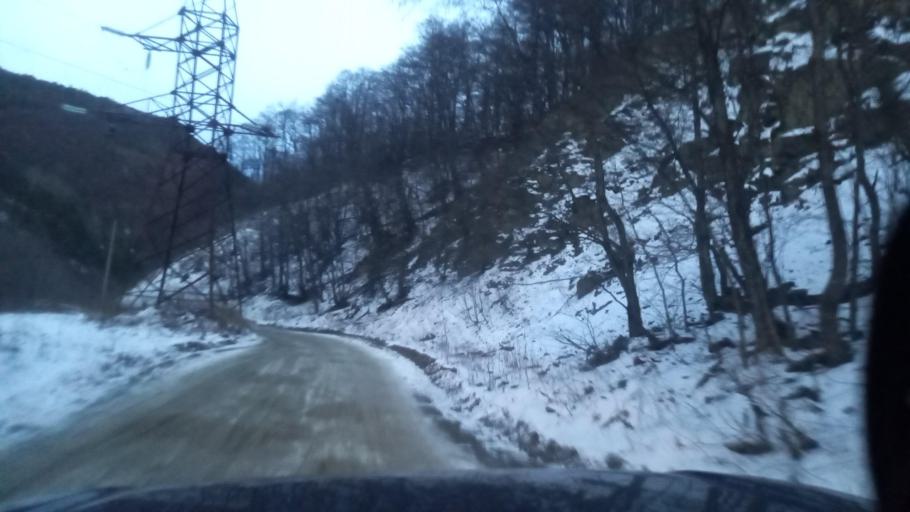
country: RU
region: Ingushetiya
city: Dzhayrakh
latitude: 42.8244
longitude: 44.5993
